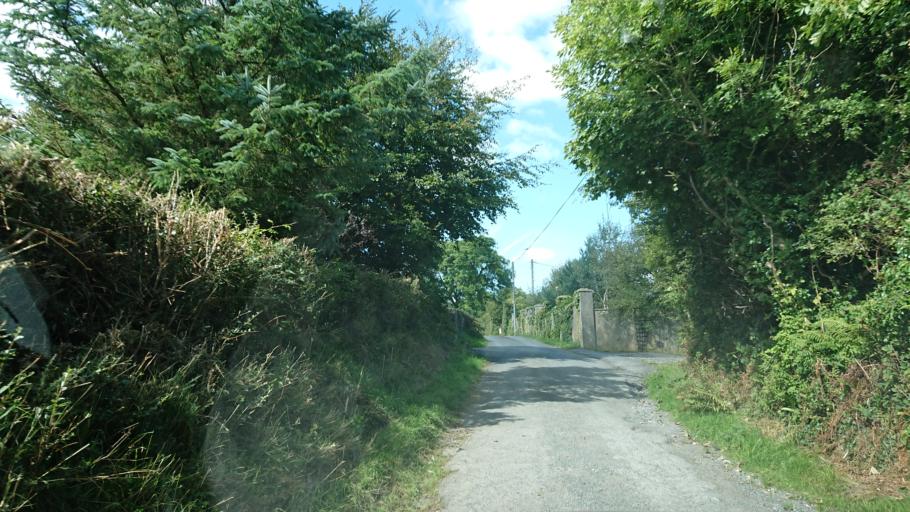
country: IE
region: Munster
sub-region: Waterford
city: Waterford
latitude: 52.2304
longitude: -7.1532
